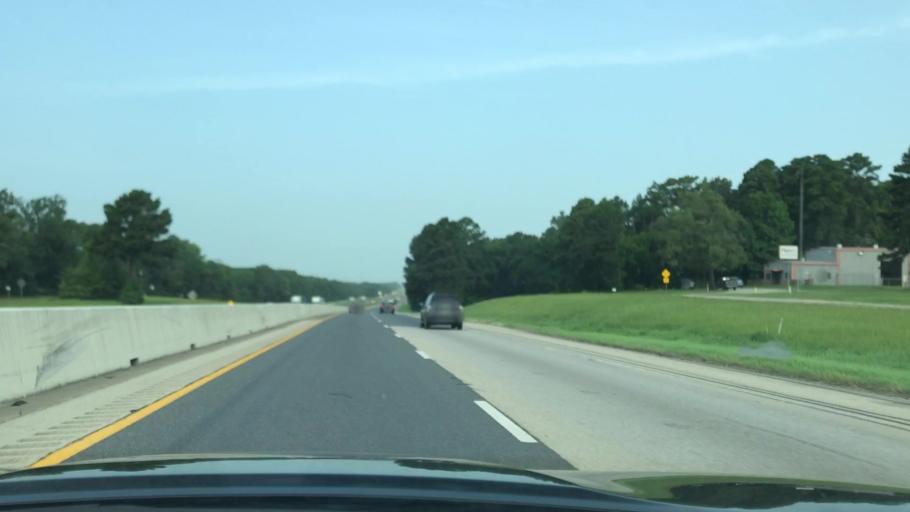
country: US
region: Texas
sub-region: Gregg County
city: Kilgore
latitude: 32.4327
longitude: -94.8673
